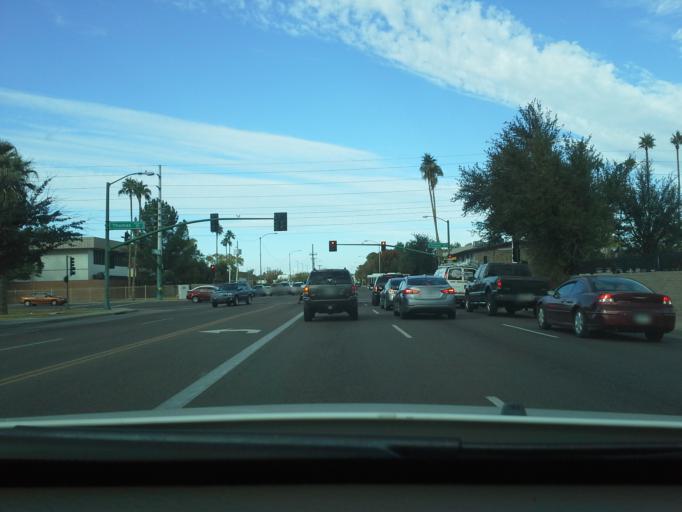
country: US
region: Arizona
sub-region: Maricopa County
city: Phoenix
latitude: 33.4800
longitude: -112.1000
